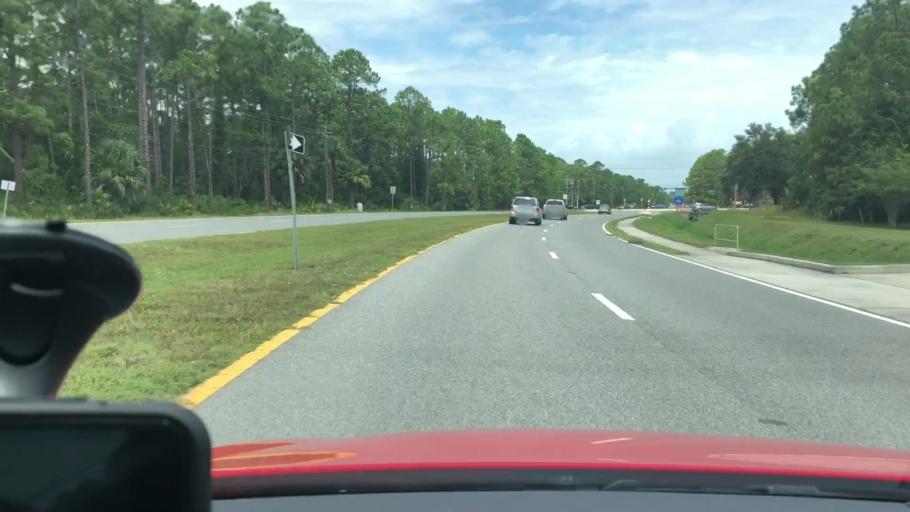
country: US
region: Florida
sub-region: Volusia County
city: Daytona Beach
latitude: 29.2072
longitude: -81.0741
